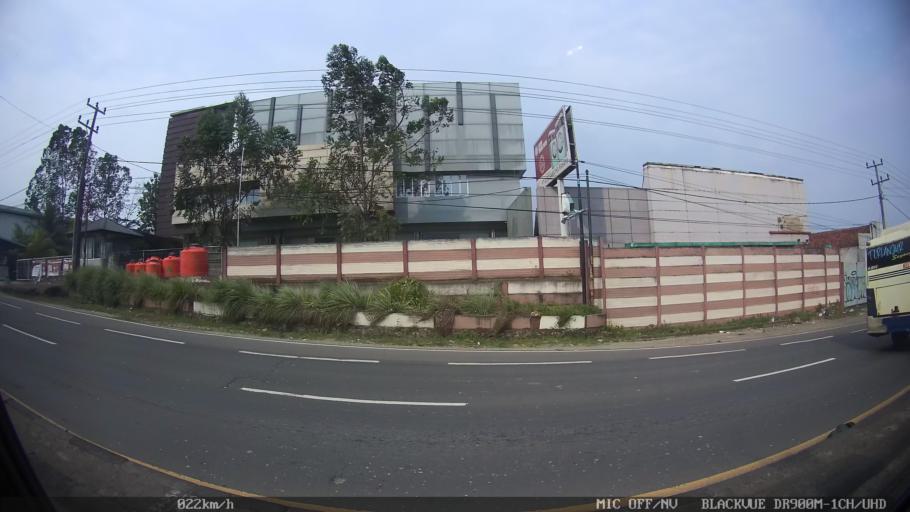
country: ID
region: Lampung
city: Kedaton
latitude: -5.3572
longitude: 105.2219
